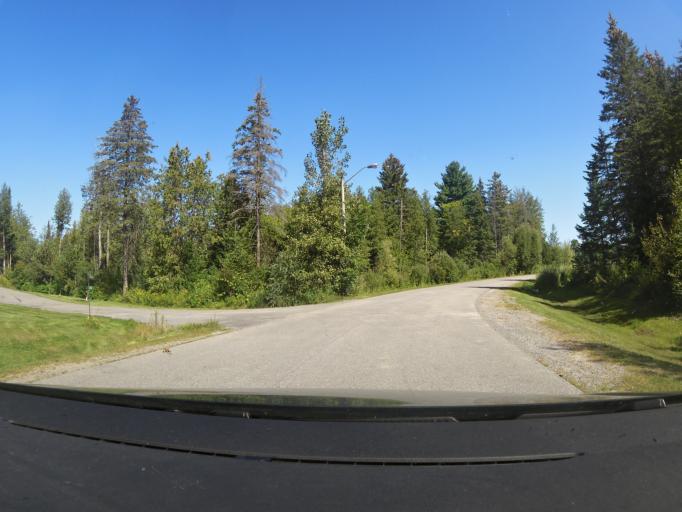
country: CA
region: Ontario
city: Bells Corners
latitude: 45.2726
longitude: -76.0003
